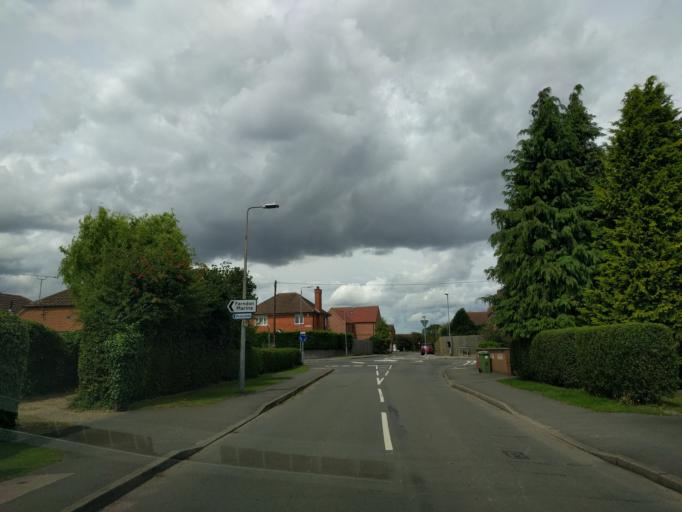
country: GB
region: England
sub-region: Nottinghamshire
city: Farndon
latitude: 53.0631
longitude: -0.8436
